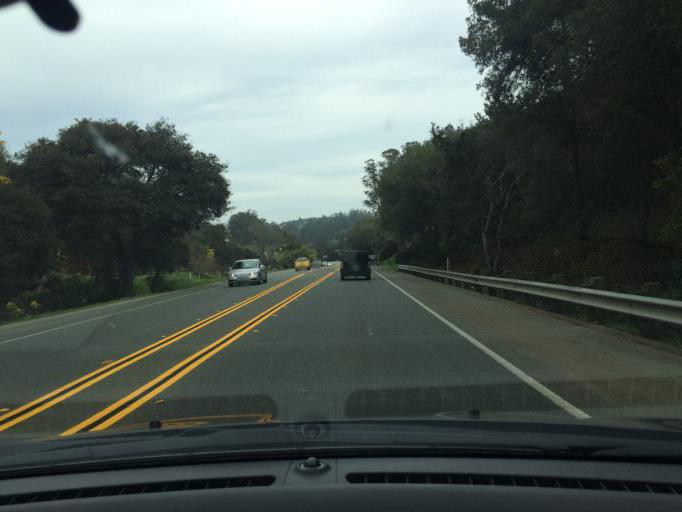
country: US
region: California
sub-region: Monterey County
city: Prunedale
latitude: 36.7884
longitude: -121.6770
